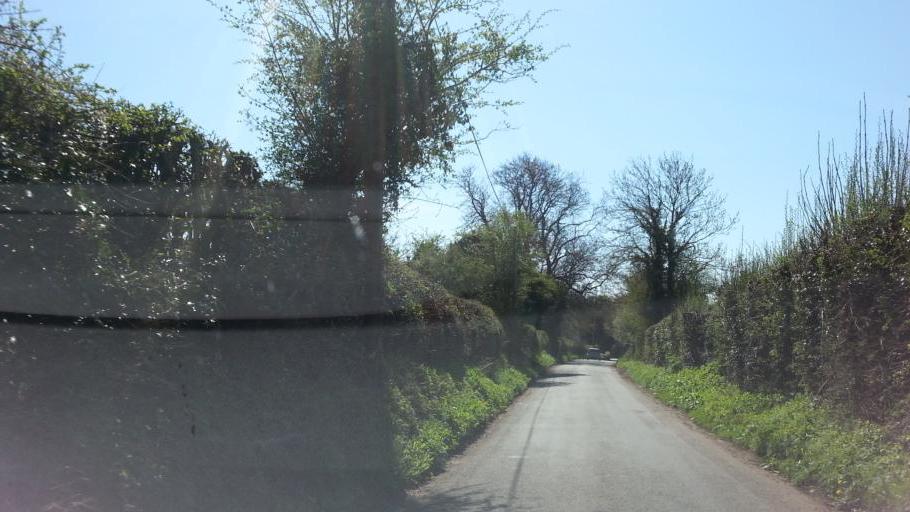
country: GB
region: England
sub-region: Staffordshire
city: Brewood
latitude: 52.6937
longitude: -2.1728
